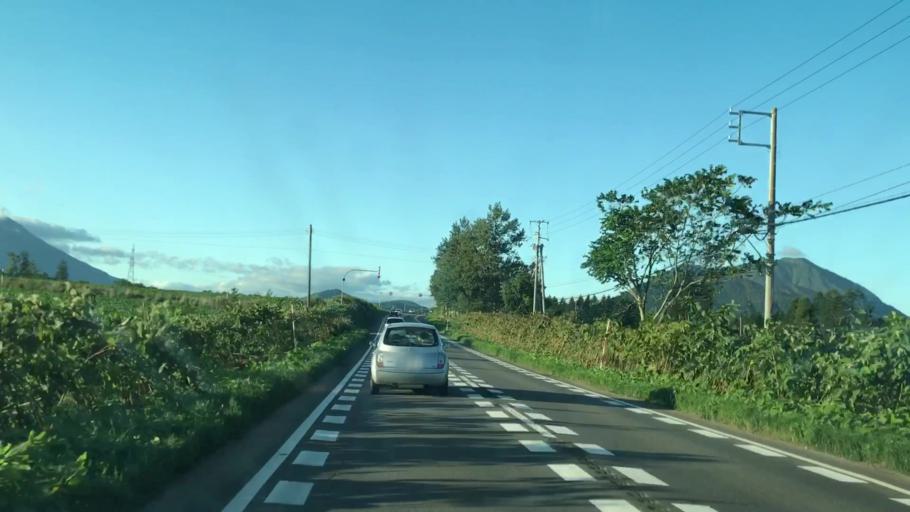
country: JP
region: Hokkaido
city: Niseko Town
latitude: 42.7150
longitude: 140.8588
